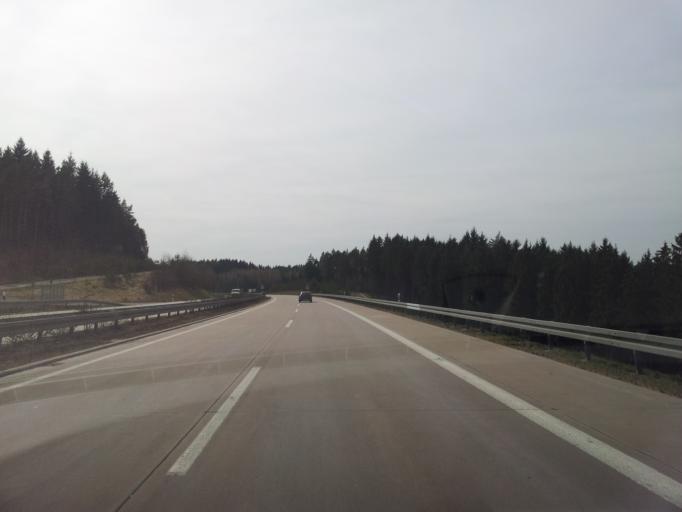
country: DE
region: Thuringia
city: Schwarza
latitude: 50.6098
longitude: 10.5518
